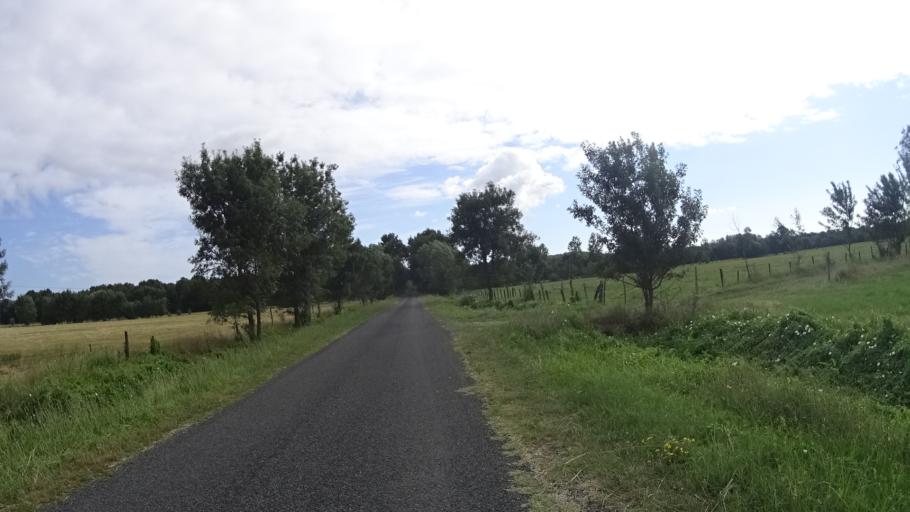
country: FR
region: Centre
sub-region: Departement d'Indre-et-Loire
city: Chouze-sur-Loire
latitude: 47.2065
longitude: 0.1098
